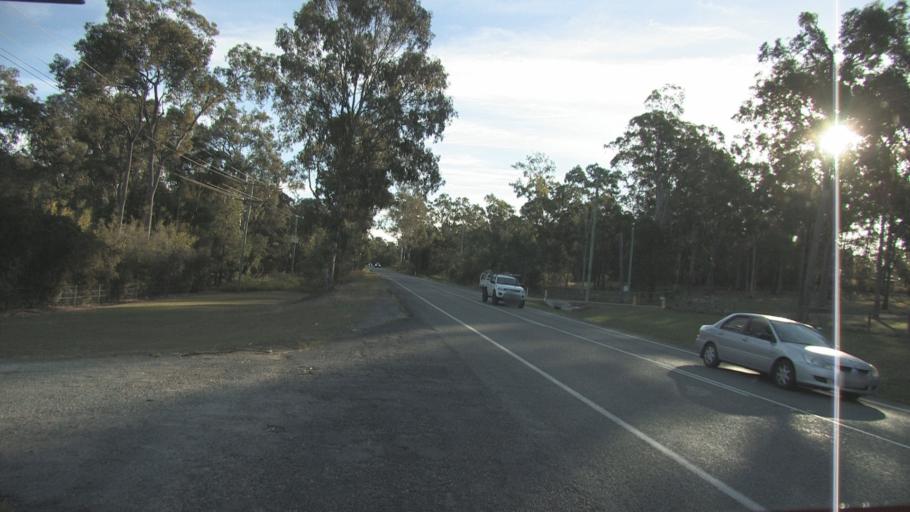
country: AU
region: Queensland
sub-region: Logan
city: North Maclean
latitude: -27.8059
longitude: 153.0543
